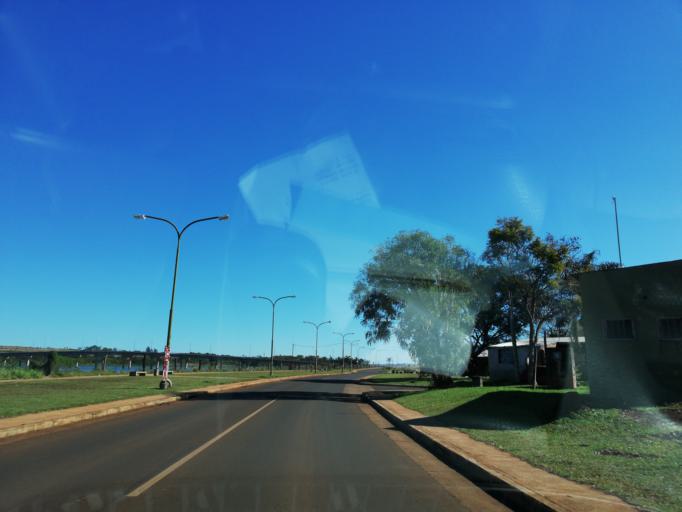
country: AR
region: Misiones
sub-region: Departamento de Capital
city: Posadas
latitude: -27.3843
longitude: -55.9520
